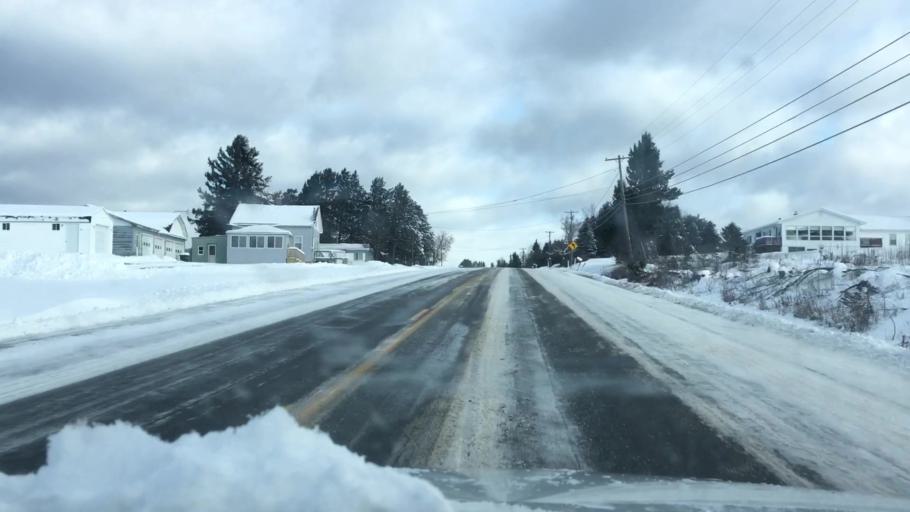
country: US
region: Maine
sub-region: Aroostook County
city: Caribou
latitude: 46.9836
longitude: -68.0322
